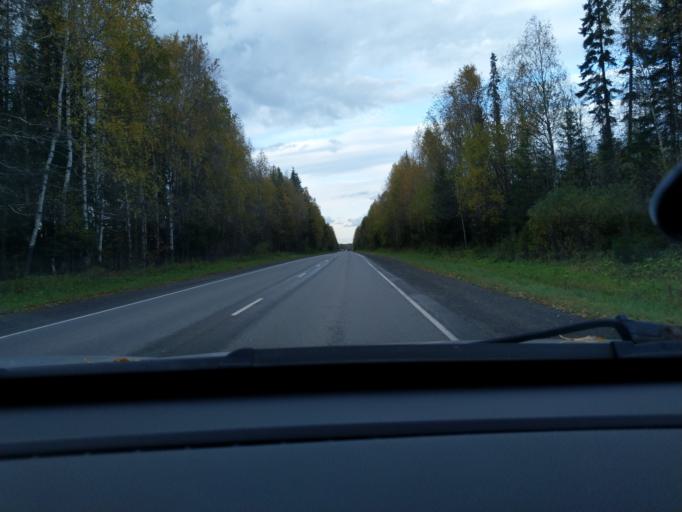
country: RU
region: Perm
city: Dobryanka
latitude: 58.4144
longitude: 56.5194
